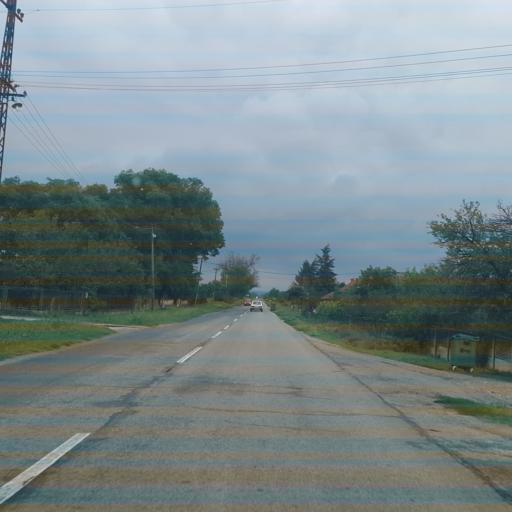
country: RS
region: Central Serbia
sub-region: Nisavski Okrug
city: Razanj
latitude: 43.6072
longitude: 21.6033
